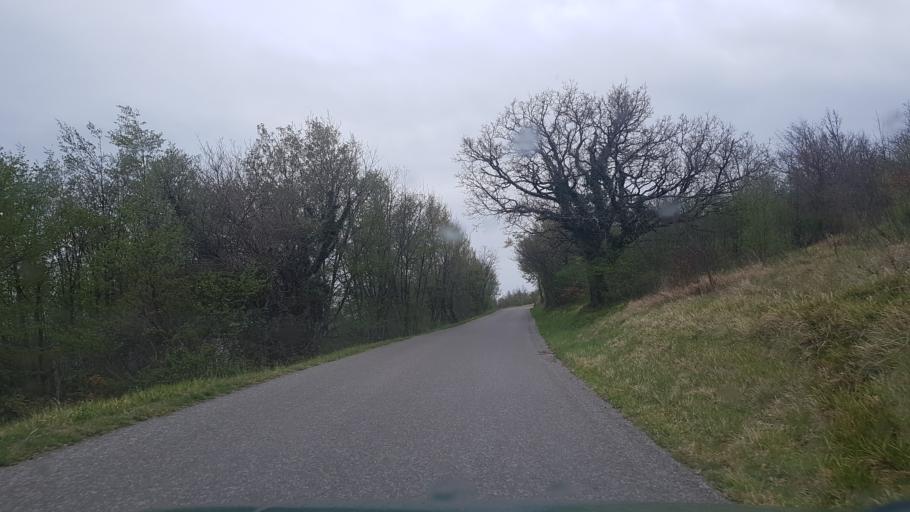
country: SI
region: Kanal
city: Deskle
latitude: 46.0413
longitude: 13.5659
